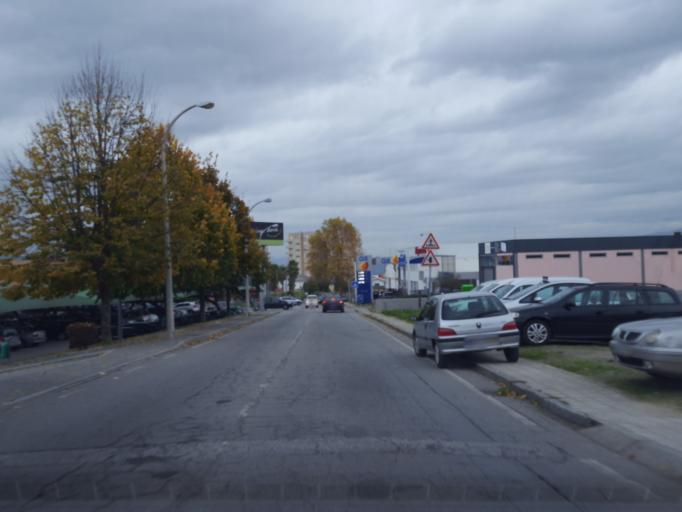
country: PT
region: Porto
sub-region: Marco de Canaveses
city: Marco de Canavezes
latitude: 41.1769
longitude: -8.1512
